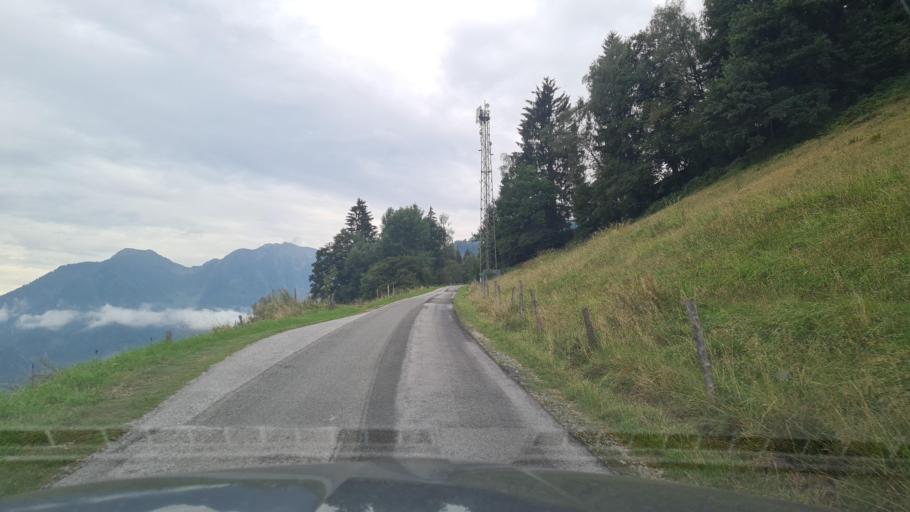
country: AT
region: Salzburg
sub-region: Politischer Bezirk Sankt Johann im Pongau
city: Sankt Johann im Pongau
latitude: 47.3571
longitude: 13.1874
